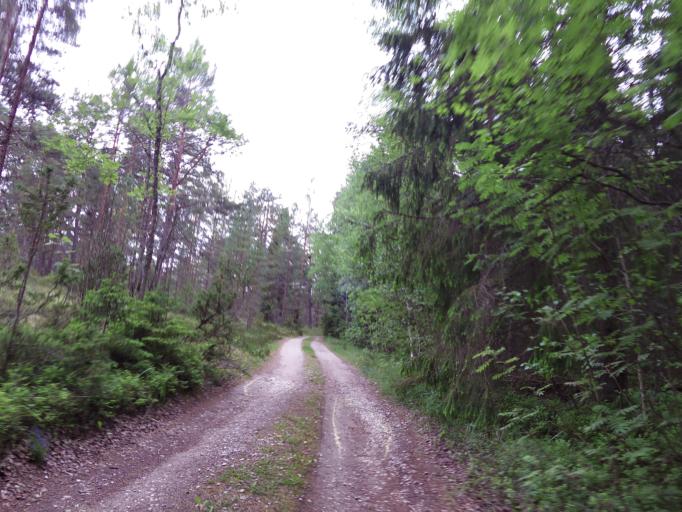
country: EE
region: Harju
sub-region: Paldiski linn
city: Paldiski
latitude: 59.2468
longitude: 23.7477
